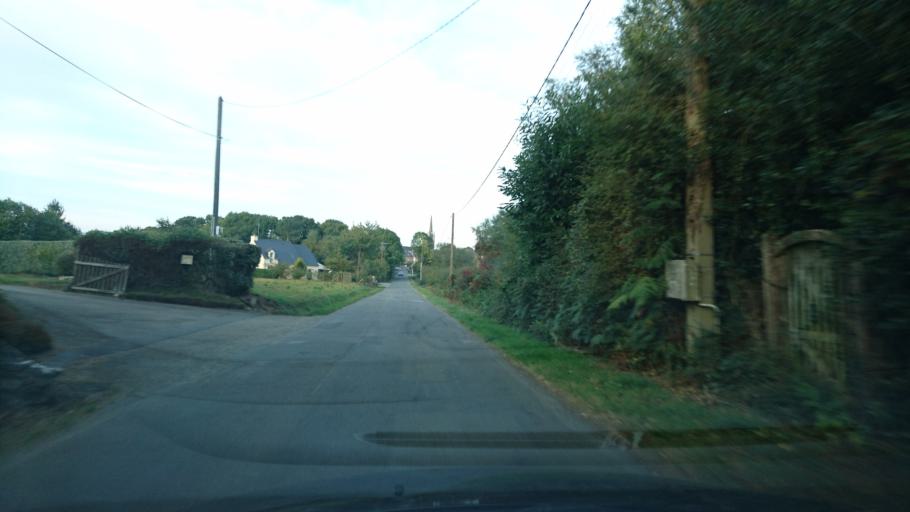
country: FR
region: Brittany
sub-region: Departement d'Ille-et-Vilaine
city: Saint-Just
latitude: 47.7623
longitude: -1.9645
